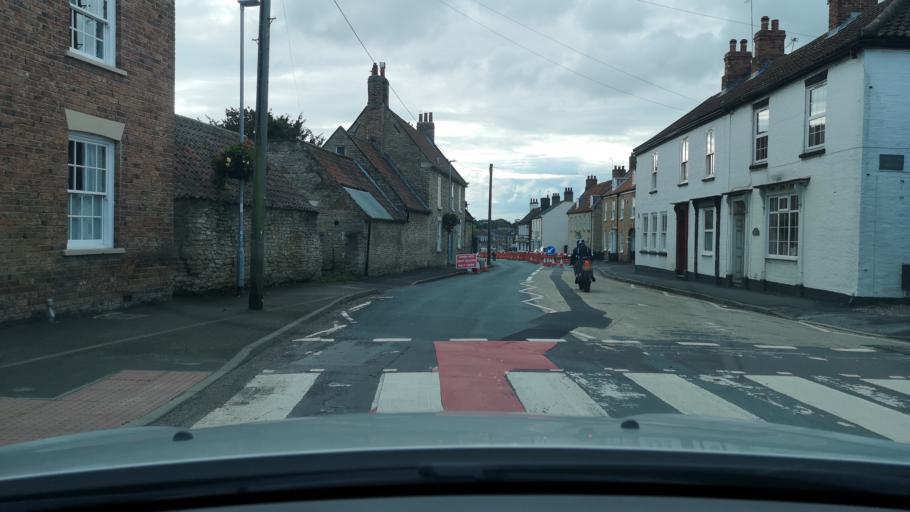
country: GB
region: England
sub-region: East Riding of Yorkshire
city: North Cave
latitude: 53.7806
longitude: -0.6448
